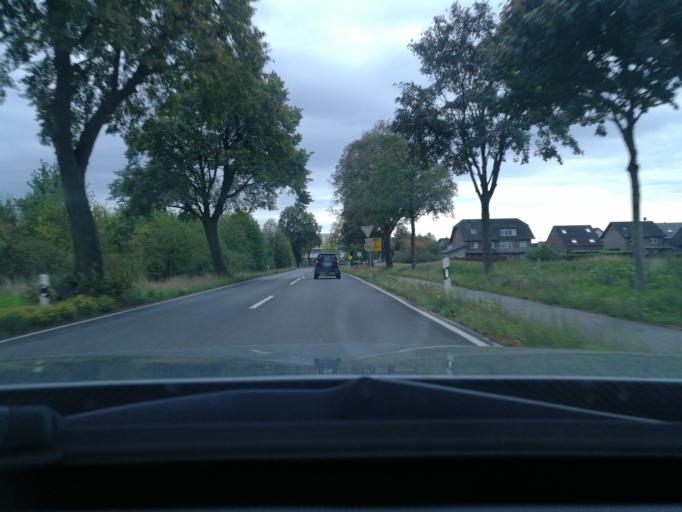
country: DE
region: North Rhine-Westphalia
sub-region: Regierungsbezirk Dusseldorf
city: Dormagen
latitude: 51.1211
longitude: 6.7664
